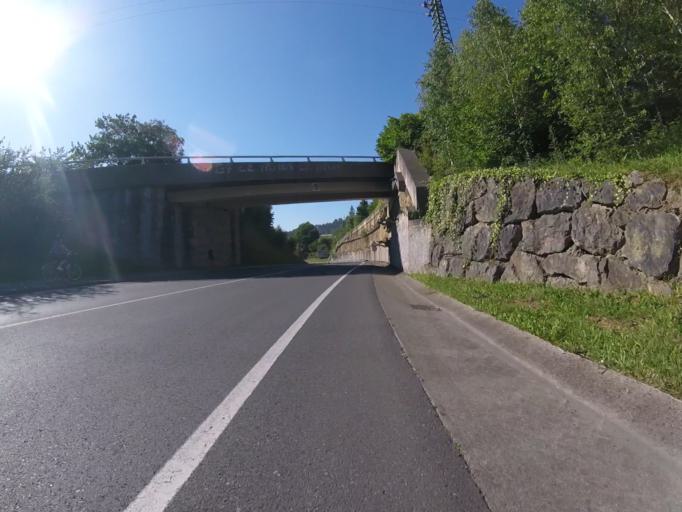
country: ES
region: Basque Country
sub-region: Provincia de Guipuzcoa
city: Azpeitia
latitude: 43.1743
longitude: -2.2583
